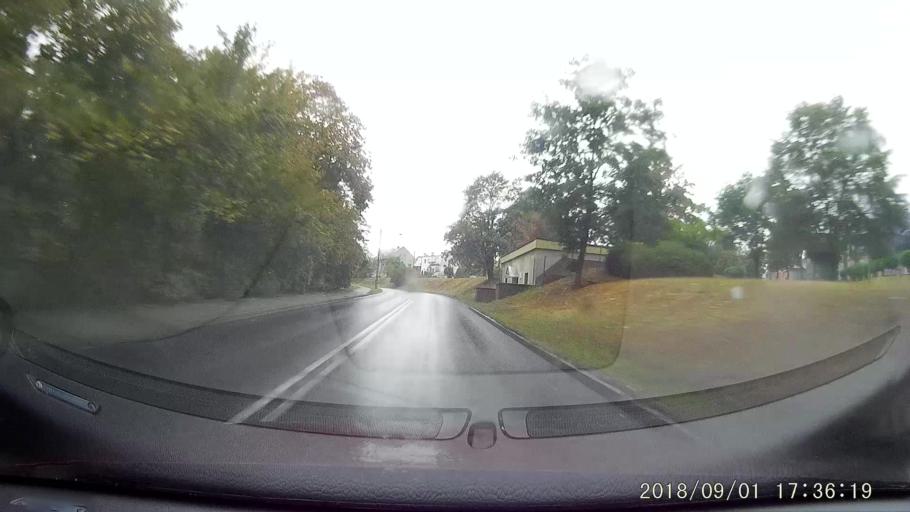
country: PL
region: Lubusz
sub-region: Powiat zaganski
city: Zagan
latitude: 51.6153
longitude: 15.3072
